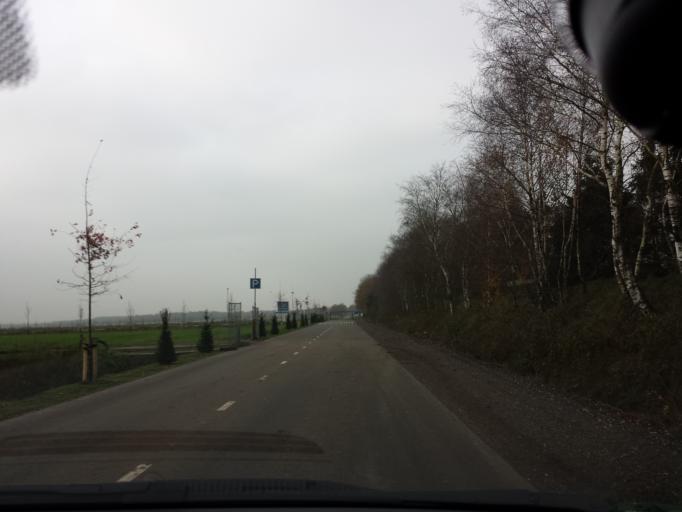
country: NL
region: North Brabant
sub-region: Gemeente Boxmeer
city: Overloon
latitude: 51.5253
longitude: 5.8771
